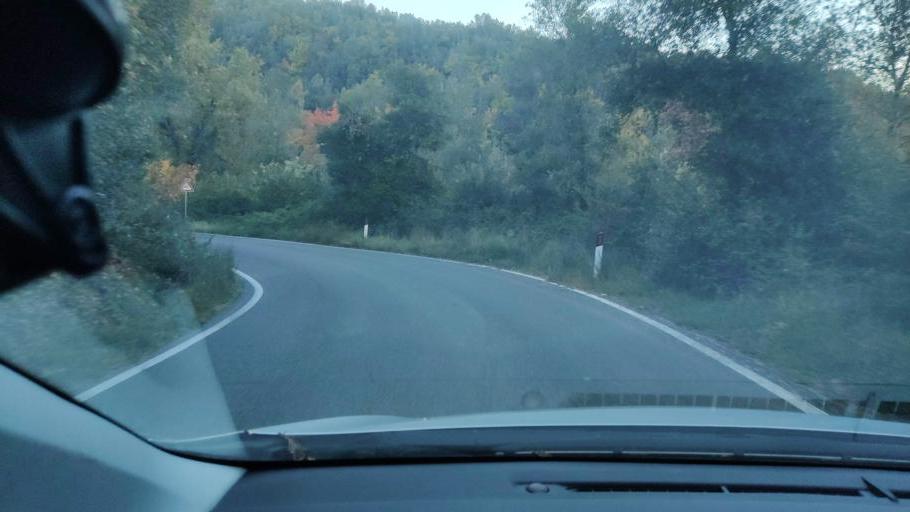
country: IT
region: Umbria
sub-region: Provincia di Terni
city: Amelia
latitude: 42.5874
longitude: 12.4307
